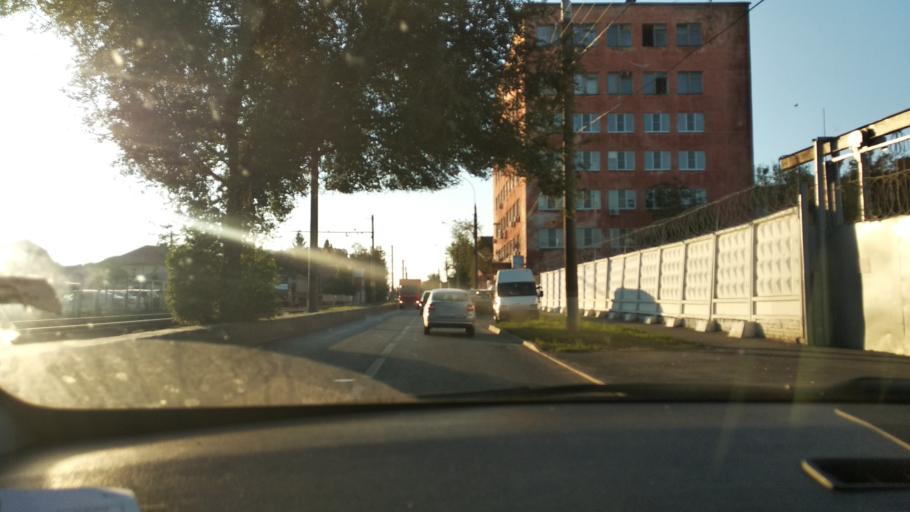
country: RU
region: Krasnodarskiy
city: Krasnodar
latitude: 45.0089
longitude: 39.0145
